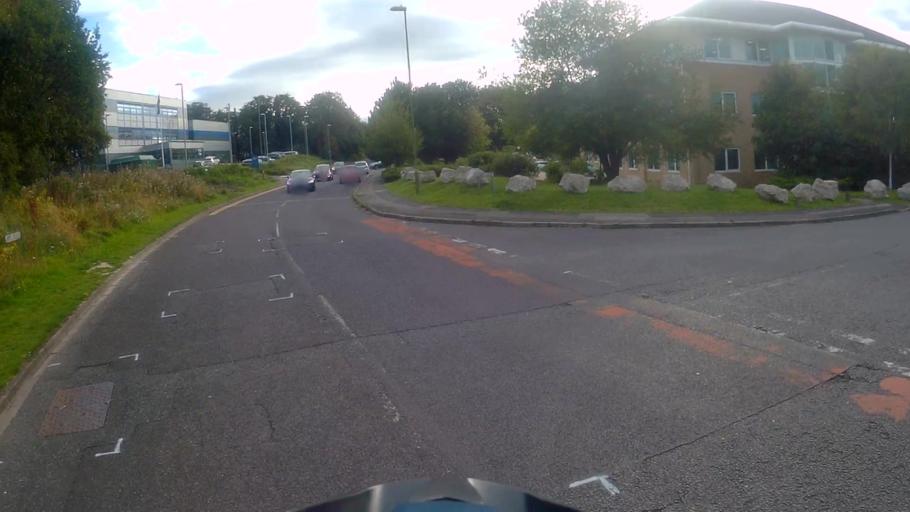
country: GB
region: England
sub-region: Hampshire
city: Basingstoke
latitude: 51.2465
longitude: -1.0952
